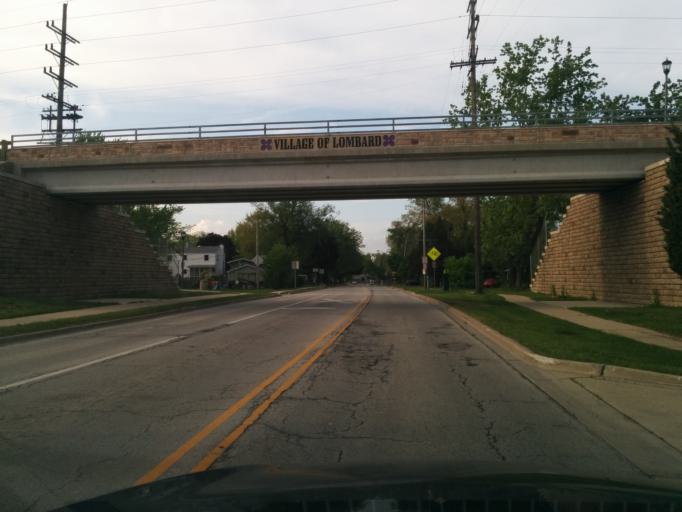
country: US
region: Illinois
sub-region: DuPage County
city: Lombard
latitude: 41.8902
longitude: -88.0084
